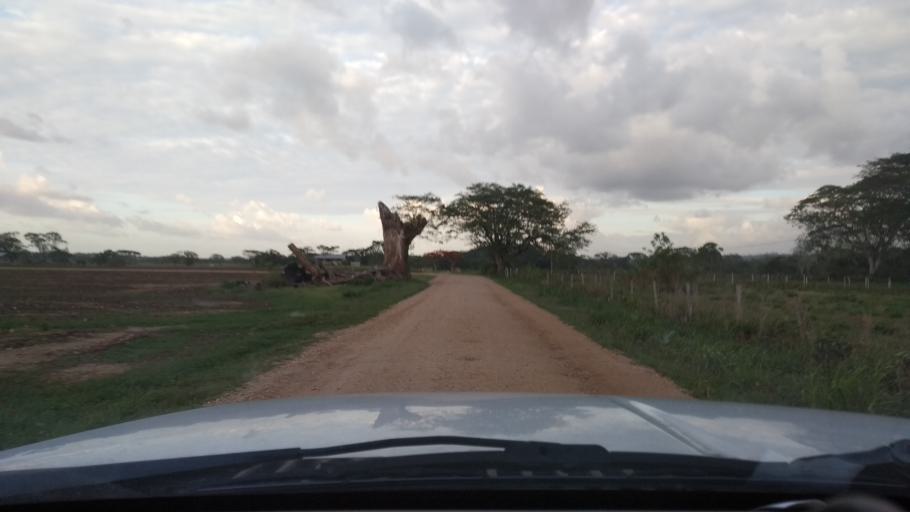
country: BZ
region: Cayo
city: San Ignacio
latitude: 17.2171
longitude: -88.9999
